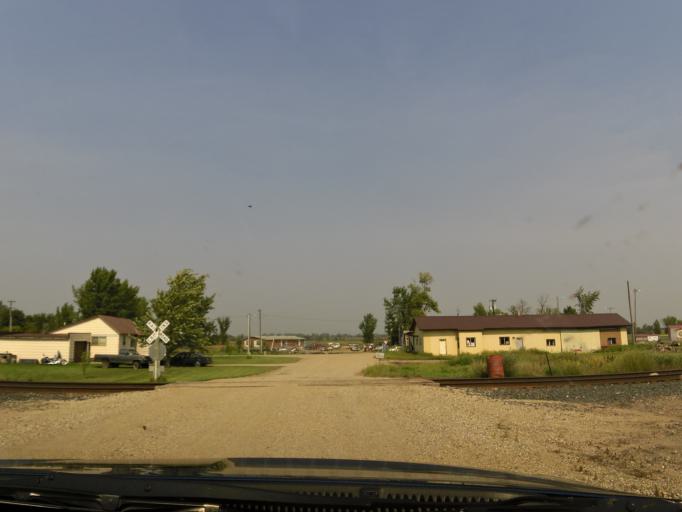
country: US
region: South Dakota
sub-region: Roberts County
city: Sisseton
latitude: 46.0783
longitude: -97.1520
